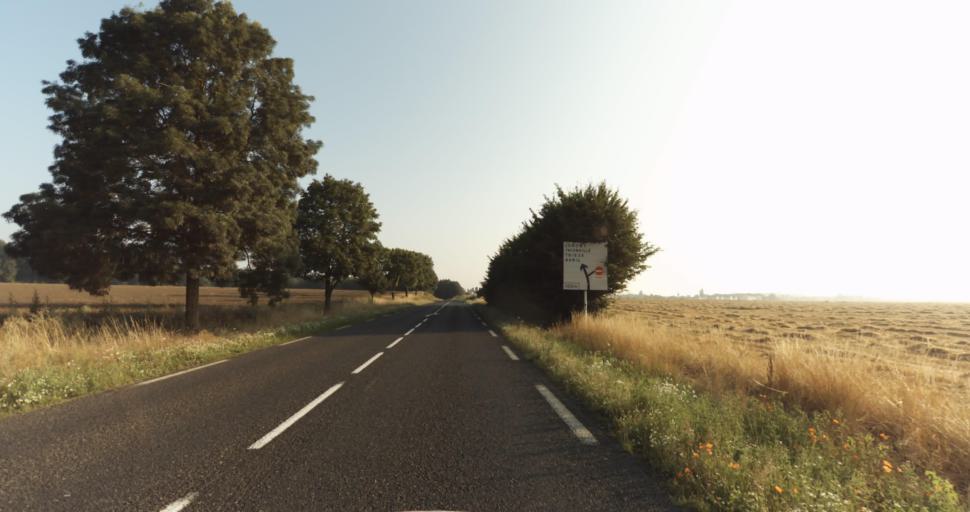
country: FR
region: Lorraine
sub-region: Departement de Meurthe-et-Moselle
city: Briey
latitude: 49.2786
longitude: 5.9595
